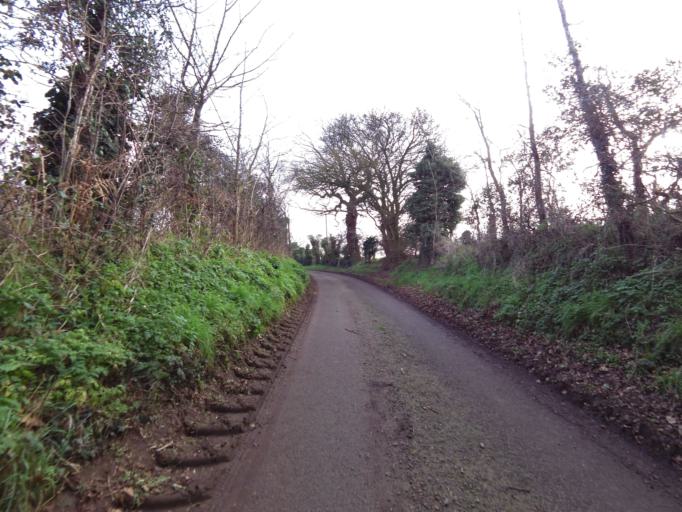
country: GB
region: England
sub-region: Suffolk
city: Woodbridge
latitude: 52.0629
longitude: 1.3090
